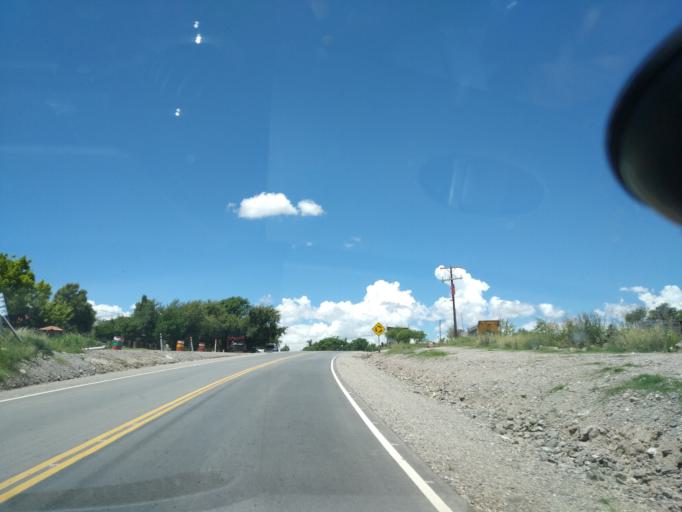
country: AR
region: Cordoba
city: Salsacate
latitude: -31.3459
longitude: -65.0818
